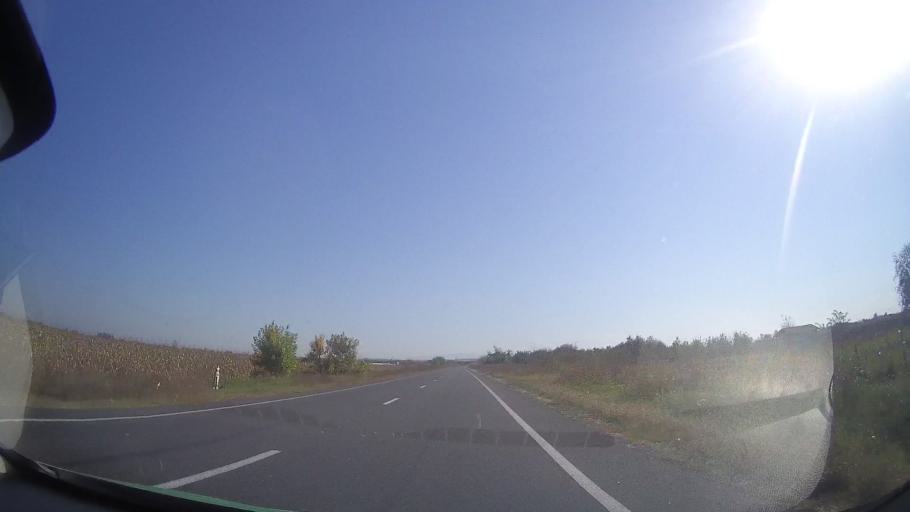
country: RO
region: Timis
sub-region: Comuna Costeiu
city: Costeiu
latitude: 45.7419
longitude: 21.8289
